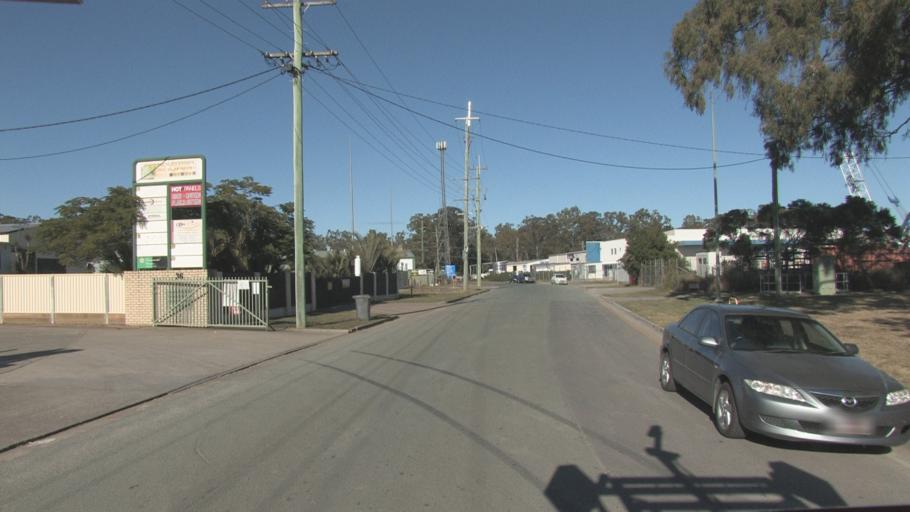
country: AU
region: Queensland
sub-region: Logan
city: Chambers Flat
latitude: -27.7695
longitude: 153.1093
